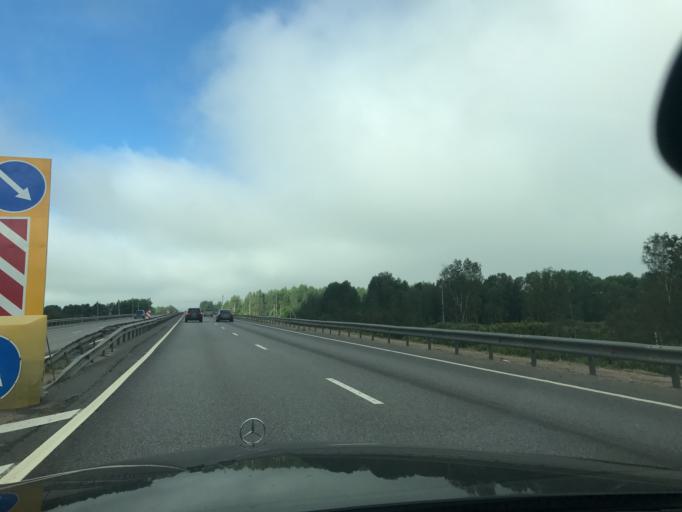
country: RU
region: Smolensk
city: Vyaz'ma
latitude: 55.2627
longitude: 34.3799
